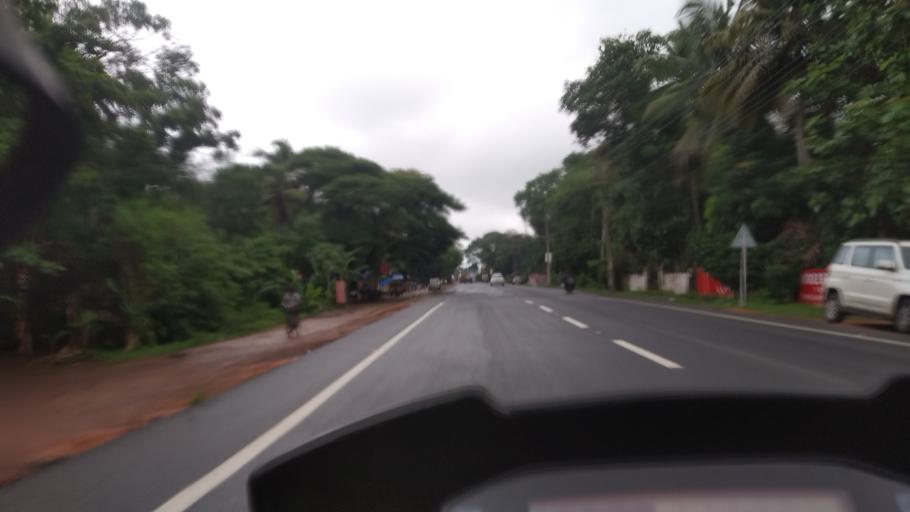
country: IN
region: Kerala
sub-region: Alappuzha
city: Mavelikara
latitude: 9.3184
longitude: 76.4217
